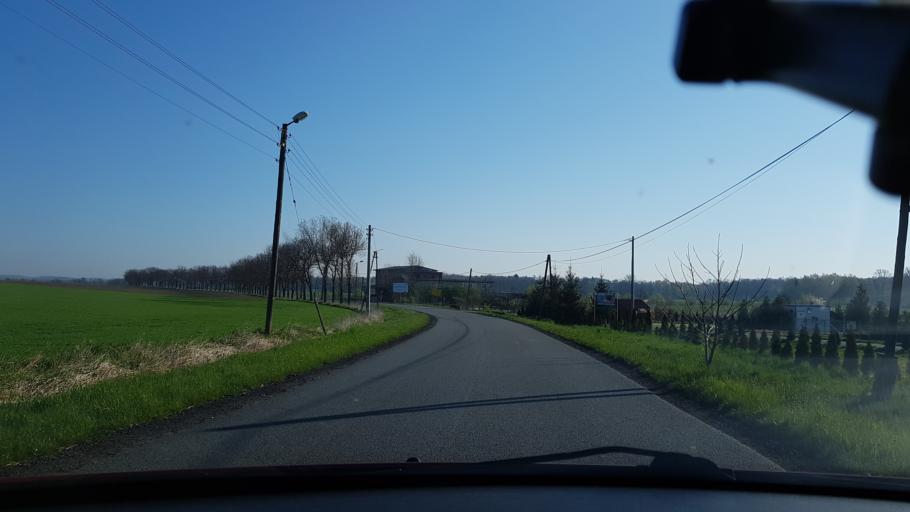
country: CZ
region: Olomoucky
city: Vidnava
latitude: 50.4081
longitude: 17.1927
